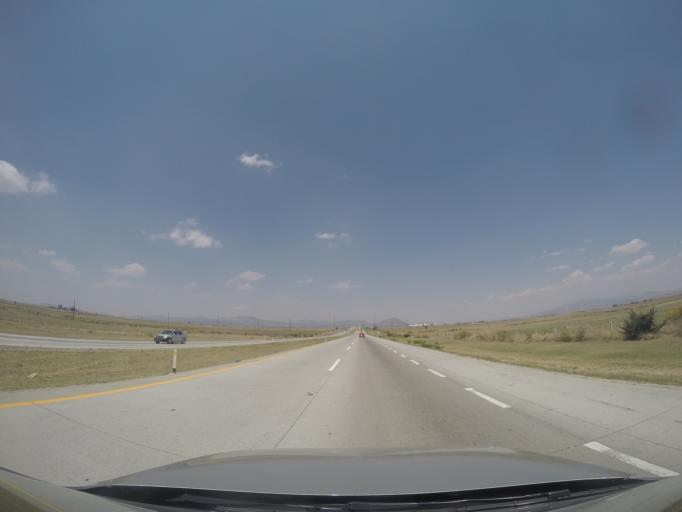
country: MX
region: Hidalgo
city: Calpulalpan
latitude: 19.6039
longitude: -98.5345
